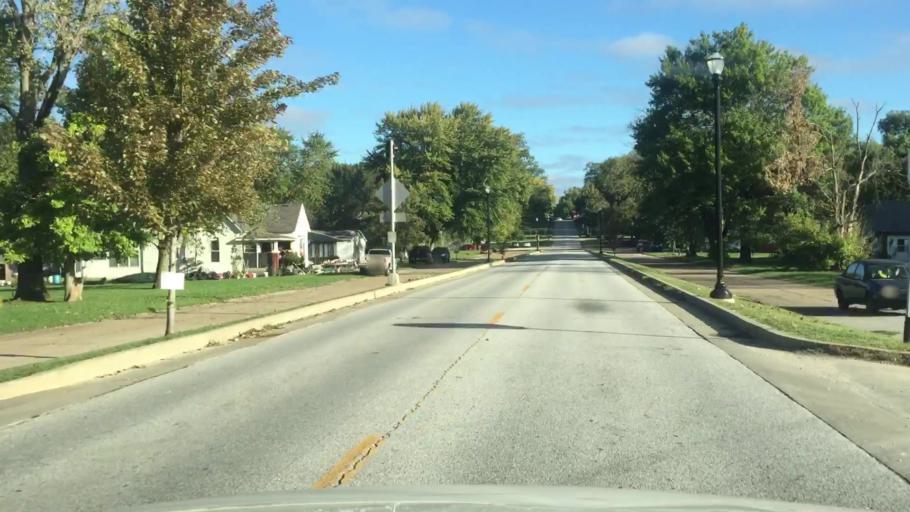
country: US
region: Missouri
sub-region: Howard County
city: New Franklin
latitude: 39.0129
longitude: -92.7377
